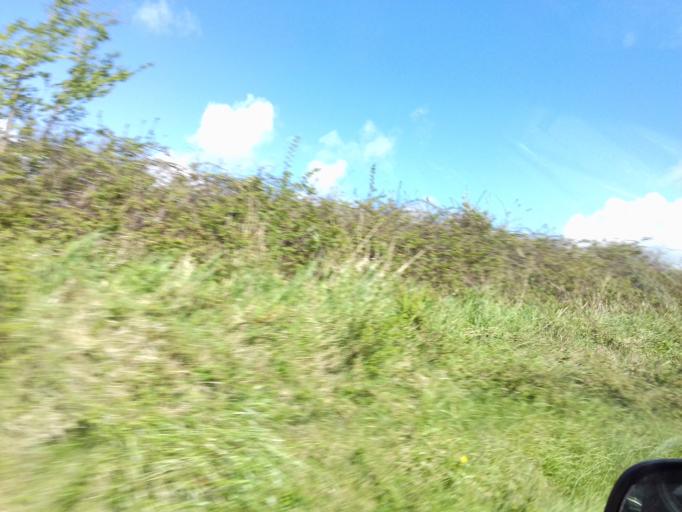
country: IE
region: Leinster
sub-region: Loch Garman
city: Castlebridge
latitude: 52.3841
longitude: -6.4207
